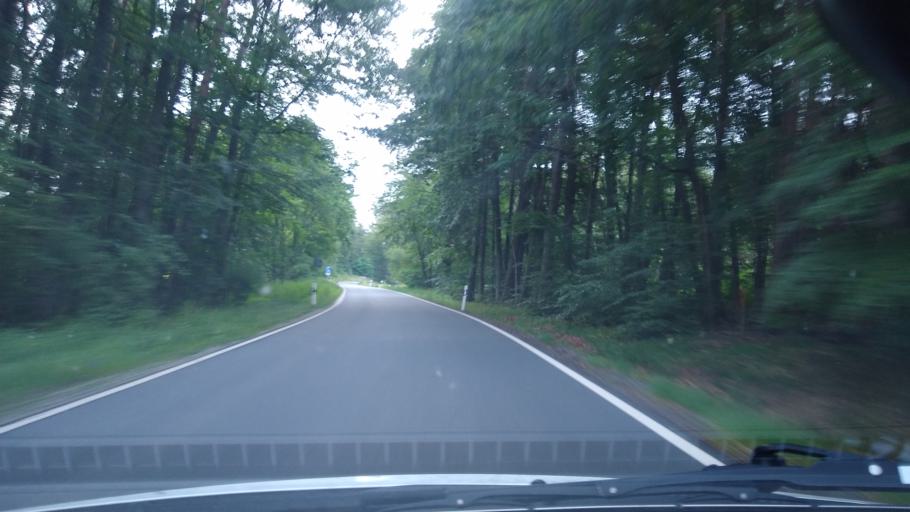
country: DE
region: Hesse
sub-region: Regierungsbezirk Darmstadt
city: Erbach
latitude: 49.6552
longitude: 8.9472
